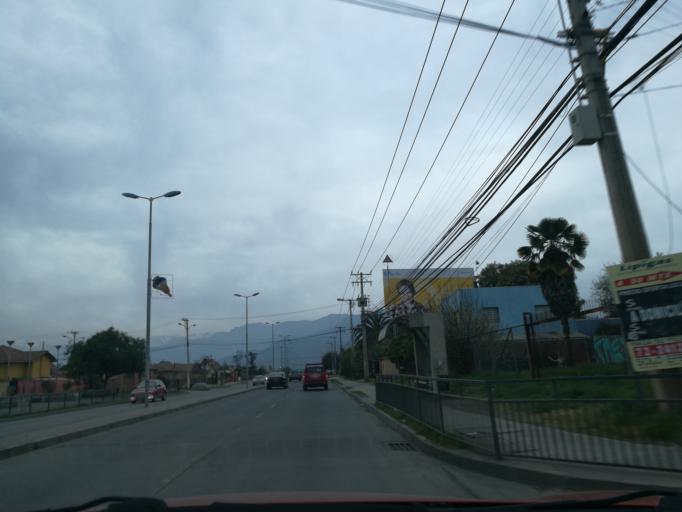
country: CL
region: O'Higgins
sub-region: Provincia de Cachapoal
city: Machali
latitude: -34.1736
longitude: -70.6883
